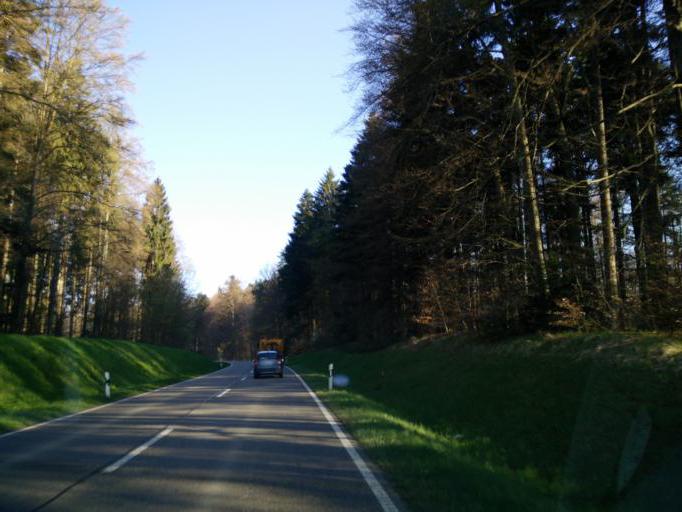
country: DE
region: Baden-Wuerttemberg
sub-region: Regierungsbezirk Stuttgart
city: Deckenpfronn
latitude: 48.6724
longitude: 8.7866
